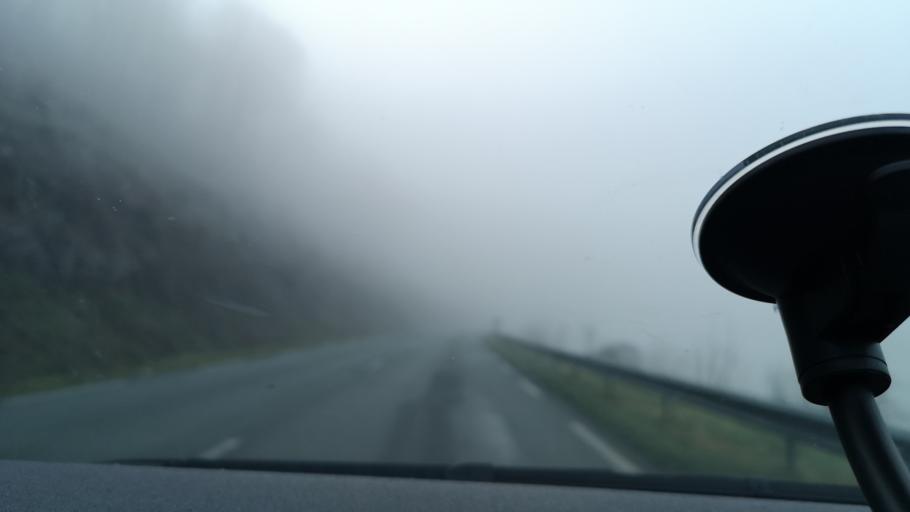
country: FR
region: Franche-Comte
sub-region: Departement du Doubs
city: Clerval
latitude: 47.4157
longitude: 6.5600
